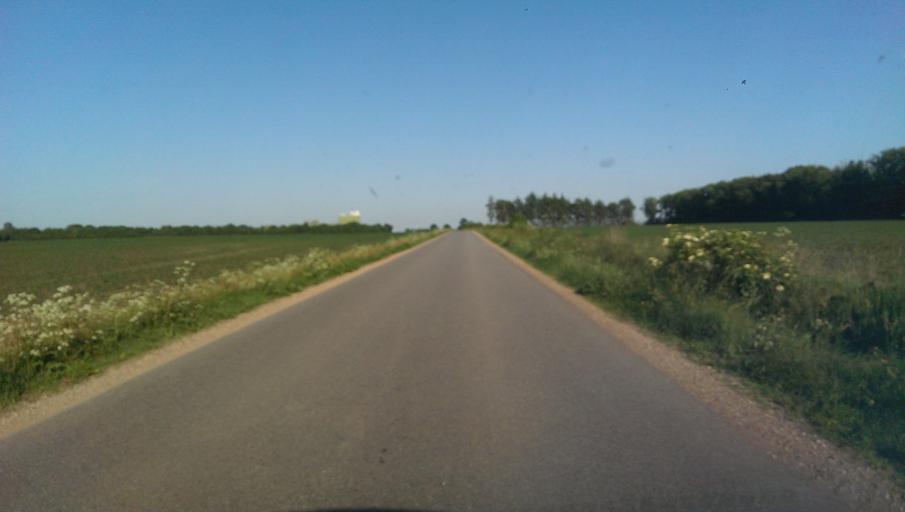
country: DK
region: South Denmark
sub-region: Esbjerg Kommune
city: Bramming
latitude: 55.5496
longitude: 8.6439
